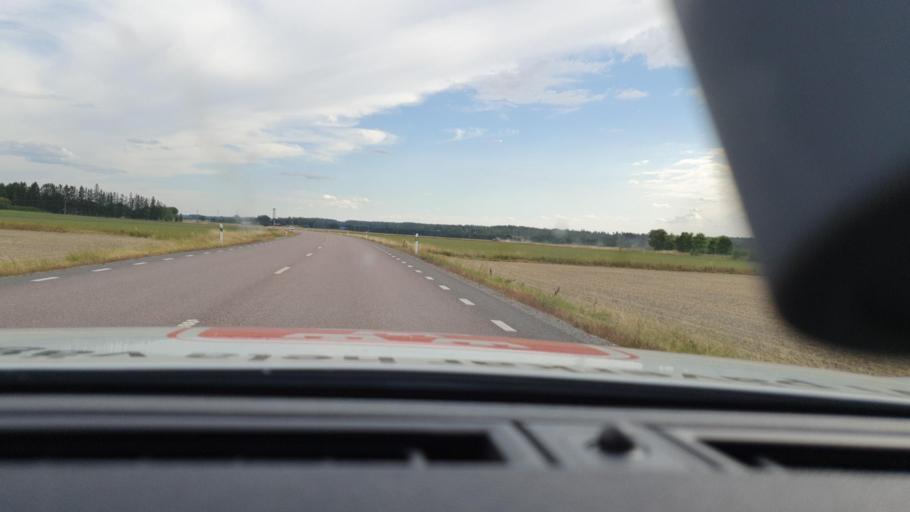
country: SE
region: Uppsala
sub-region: Osthammars Kommun
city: Bjorklinge
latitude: 59.9233
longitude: 17.5000
